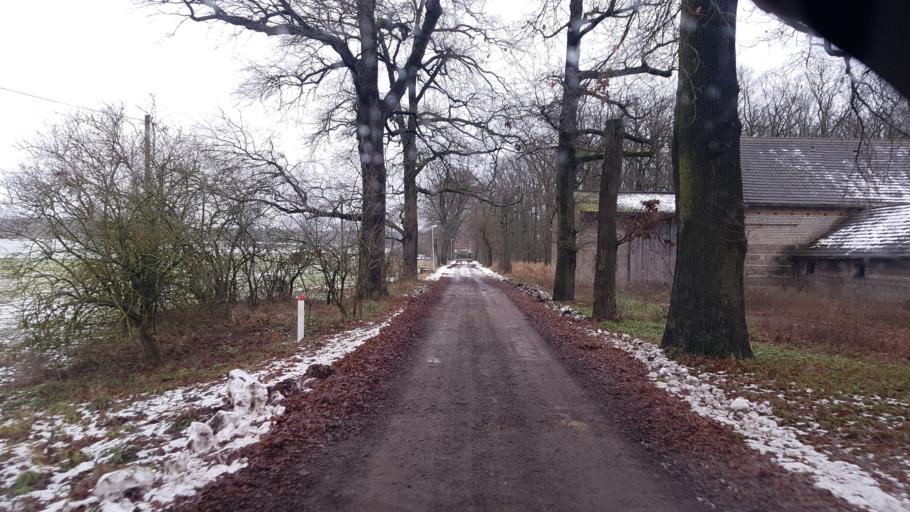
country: DE
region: Brandenburg
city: Schenkendobern
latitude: 51.9669
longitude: 14.5802
